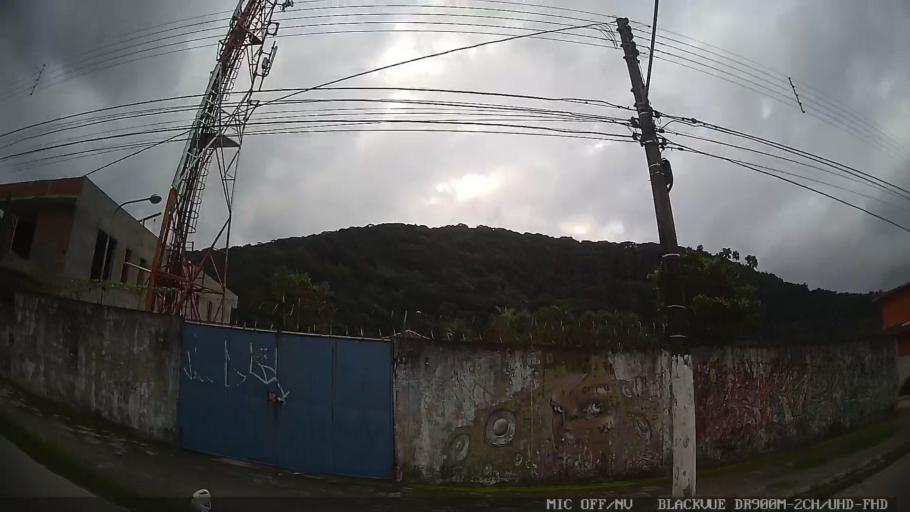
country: BR
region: Sao Paulo
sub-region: Guaruja
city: Guaruja
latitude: -24.0145
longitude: -46.2864
